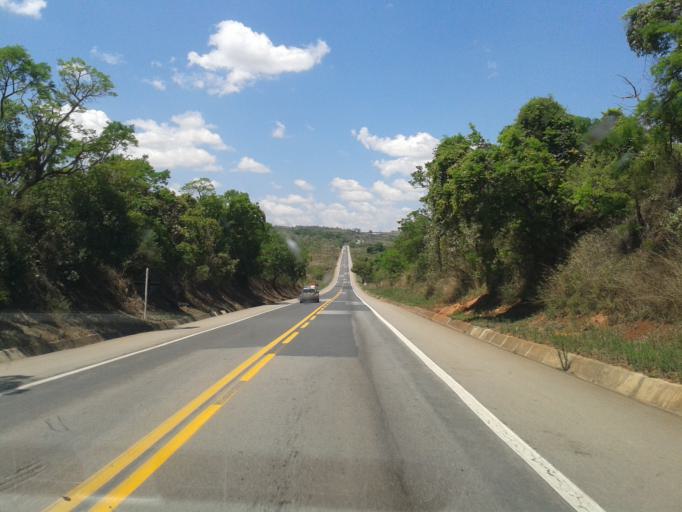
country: BR
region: Minas Gerais
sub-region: Ibia
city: Ibia
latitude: -19.5664
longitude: -46.6494
